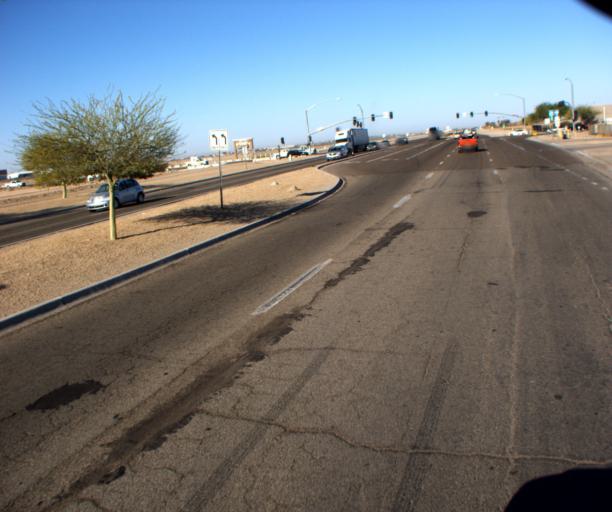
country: US
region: Arizona
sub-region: Yuma County
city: Yuma
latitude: 32.6698
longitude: -114.5801
